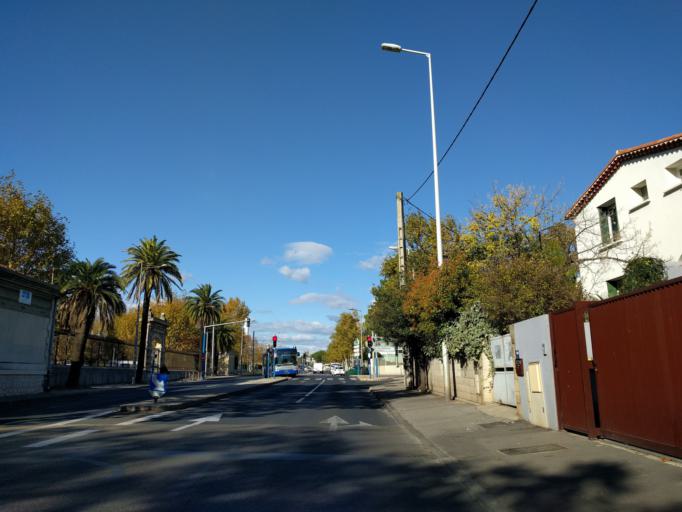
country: FR
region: Languedoc-Roussillon
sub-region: Departement de l'Herault
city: Montpellier
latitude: 43.6275
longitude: 3.8587
